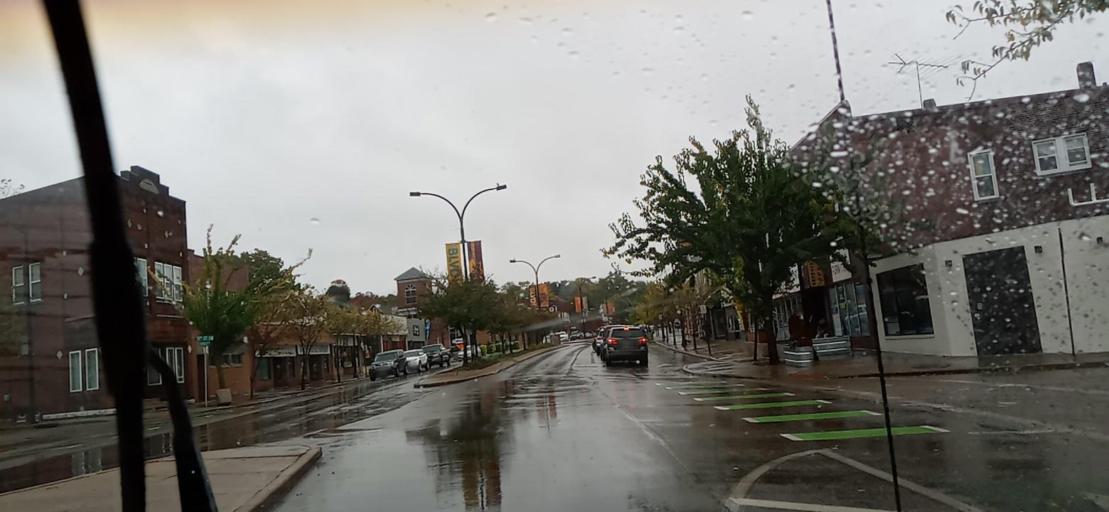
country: US
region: Ohio
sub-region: Summit County
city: Portage Lakes
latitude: 41.0431
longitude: -81.5597
